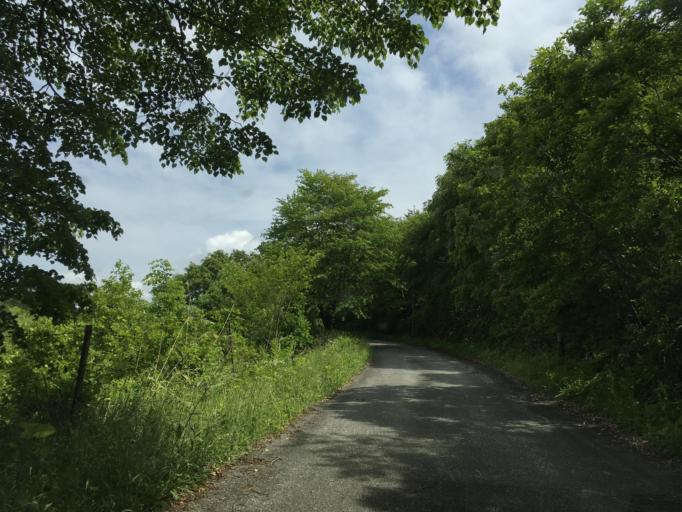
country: JP
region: Iwate
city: Mizusawa
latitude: 39.1341
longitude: 141.3155
